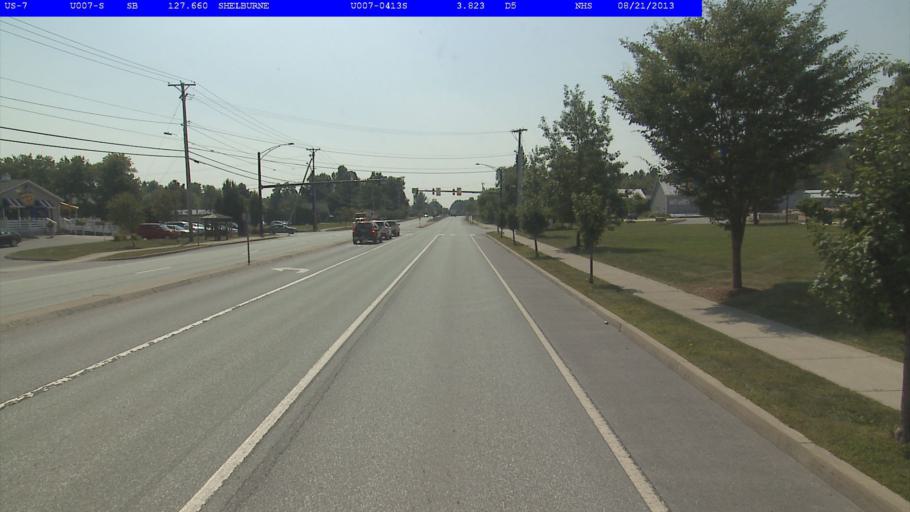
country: US
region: Vermont
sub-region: Chittenden County
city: Burlington
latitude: 44.3970
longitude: -73.2197
